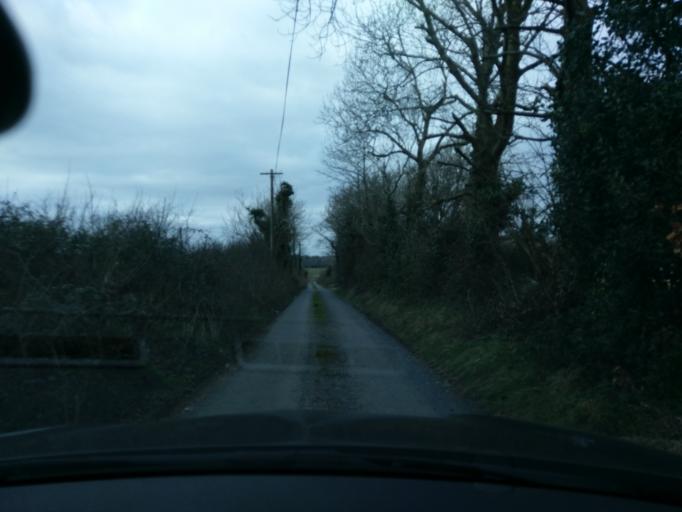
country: IE
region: Connaught
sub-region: County Galway
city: Oranmore
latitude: 53.2125
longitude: -8.8626
